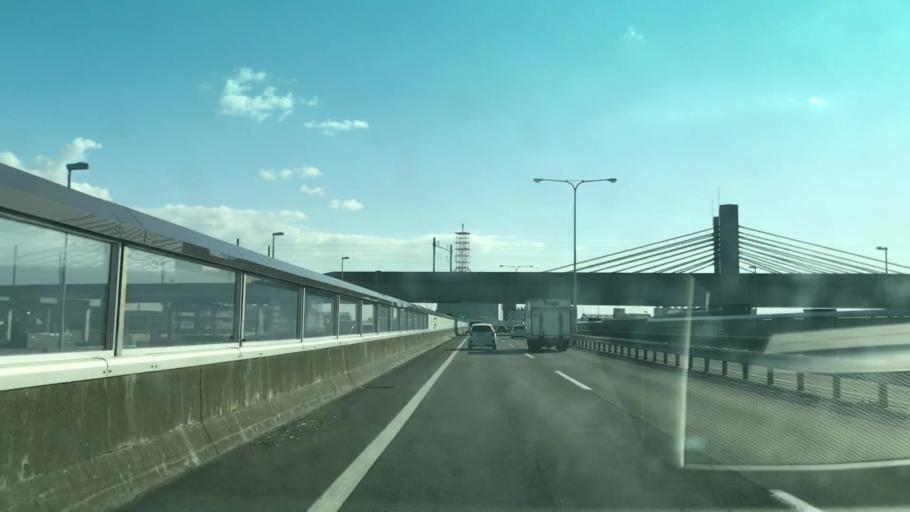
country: JP
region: Hokkaido
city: Sapporo
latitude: 43.1019
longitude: 141.3247
